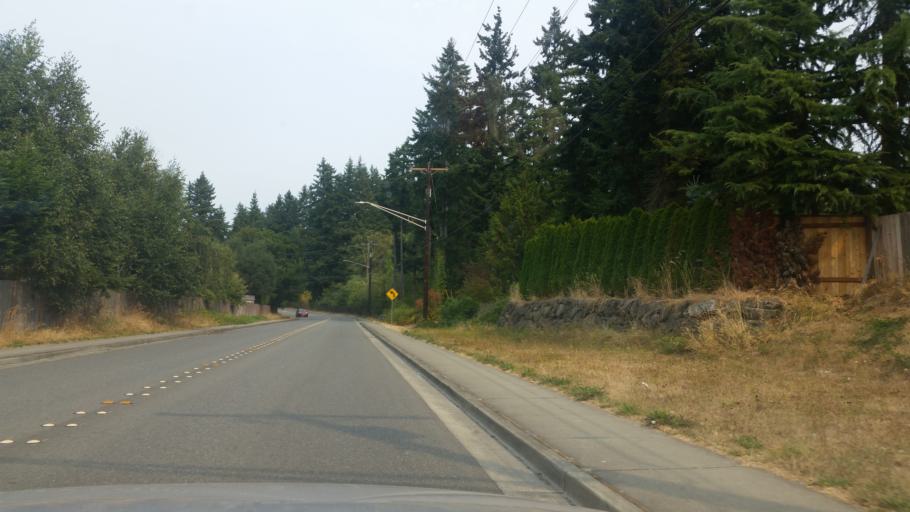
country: US
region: Washington
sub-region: Snohomish County
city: Lynnwood
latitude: 47.8344
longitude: -122.3271
